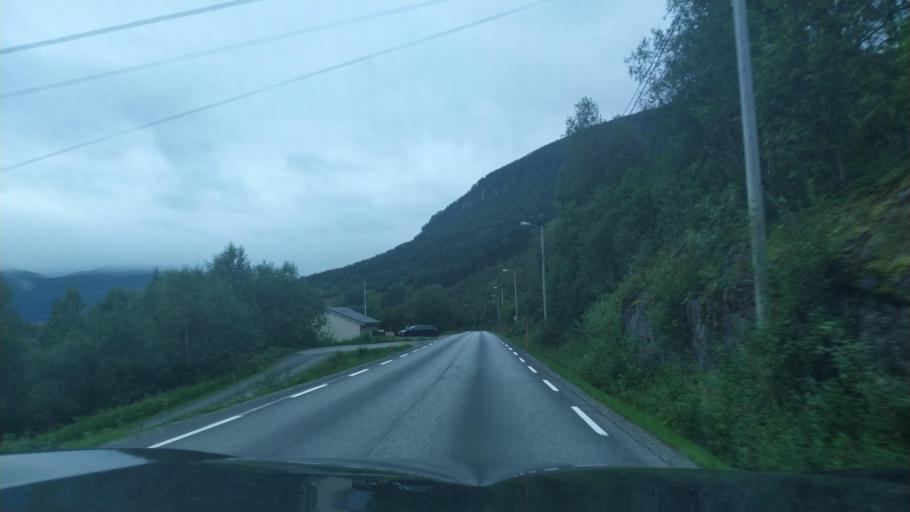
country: NO
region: Troms
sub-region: Lavangen
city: Tennevoll
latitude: 68.7433
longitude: 17.8170
